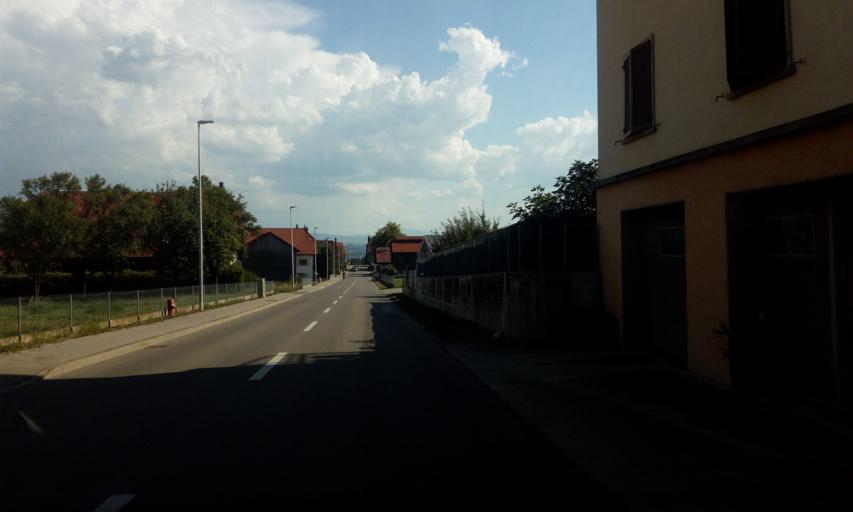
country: CH
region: Fribourg
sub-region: Broye District
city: Domdidier
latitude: 46.8948
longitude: 6.9754
